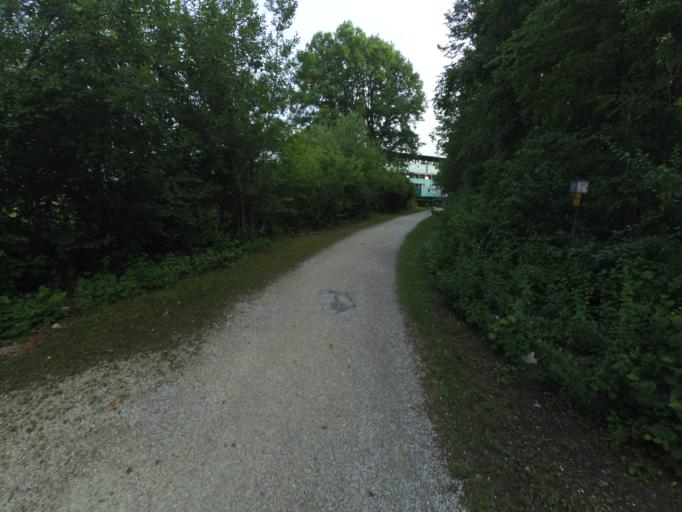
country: DE
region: Baden-Wuerttemberg
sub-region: Tuebingen Region
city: Dornstadt
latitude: 48.4196
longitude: 9.9478
